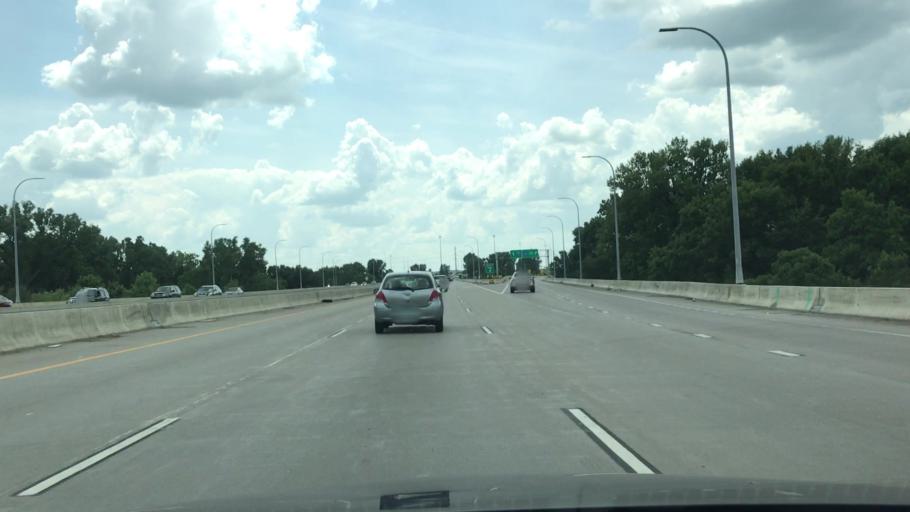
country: US
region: Minnesota
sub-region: Scott County
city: Savage
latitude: 44.7946
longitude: -93.3994
